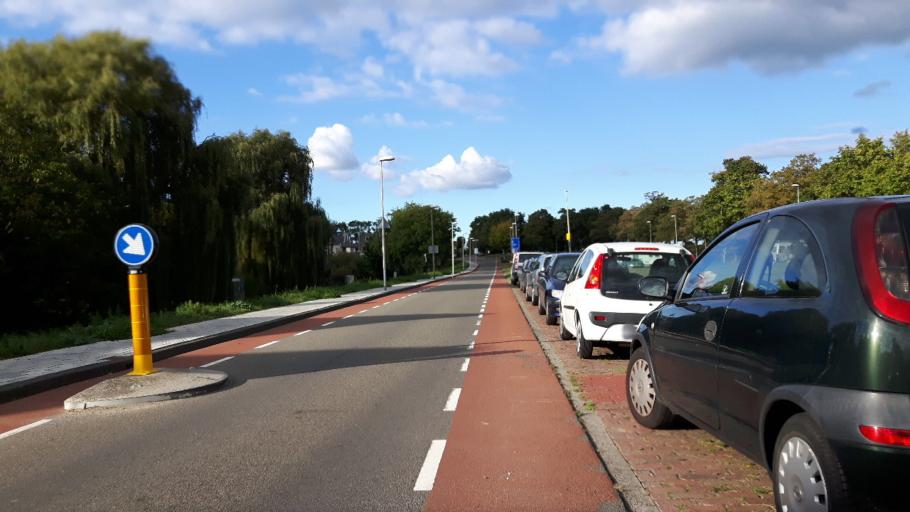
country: NL
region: Utrecht
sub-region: Gemeente Vianen
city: Vianen
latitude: 51.9942
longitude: 5.0960
